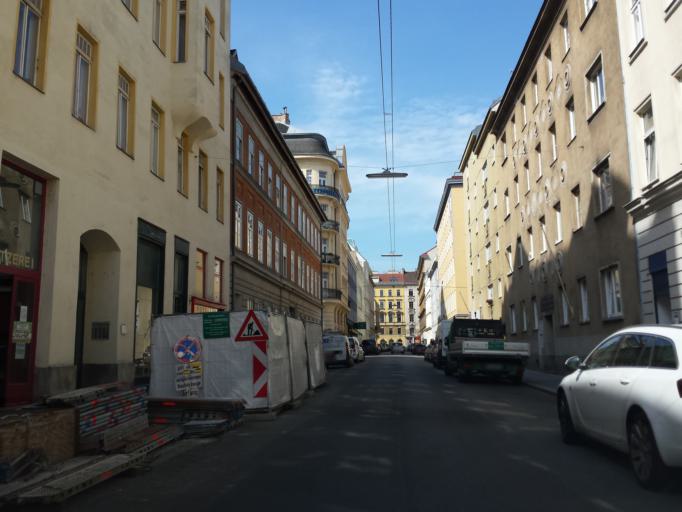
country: AT
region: Vienna
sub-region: Wien Stadt
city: Vienna
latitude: 48.1901
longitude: 16.3747
